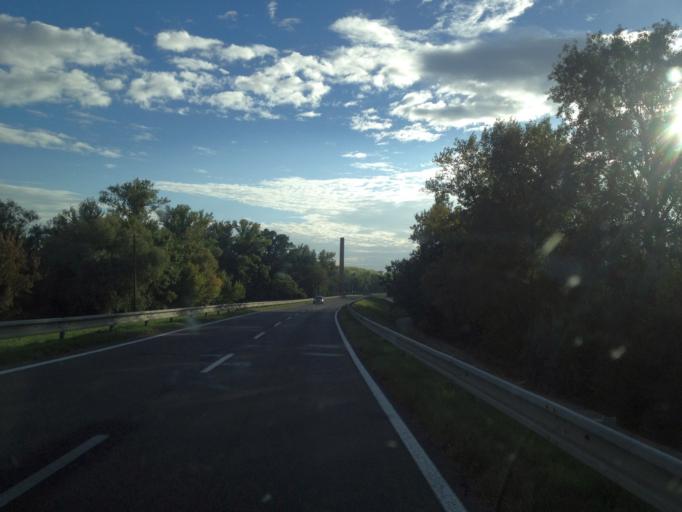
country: HU
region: Komarom-Esztergom
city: Dunaalmas
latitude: 47.7453
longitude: 18.3289
